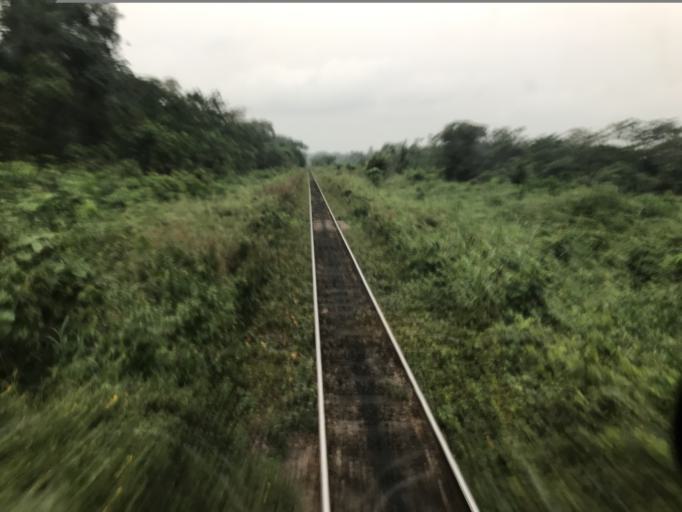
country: CM
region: Littoral
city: Edea
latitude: 3.9103
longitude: 10.1042
